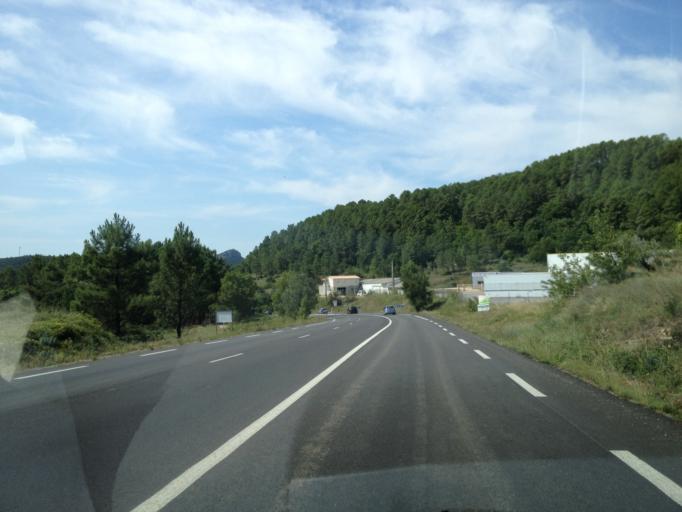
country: FR
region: Languedoc-Roussillon
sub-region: Departement du Gard
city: Les Mages
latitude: 44.2326
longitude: 4.1632
